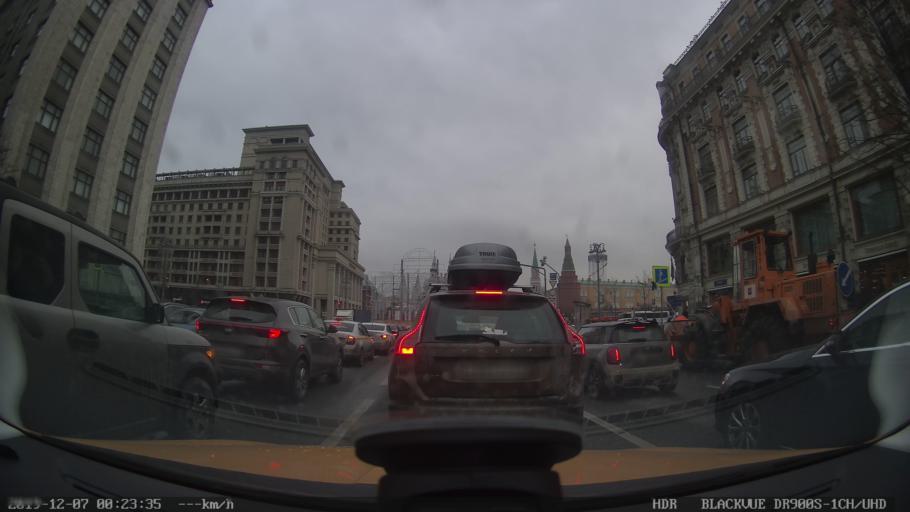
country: RU
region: Moscow
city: Zapadnoye Degunino
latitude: 55.8538
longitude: 37.5243
